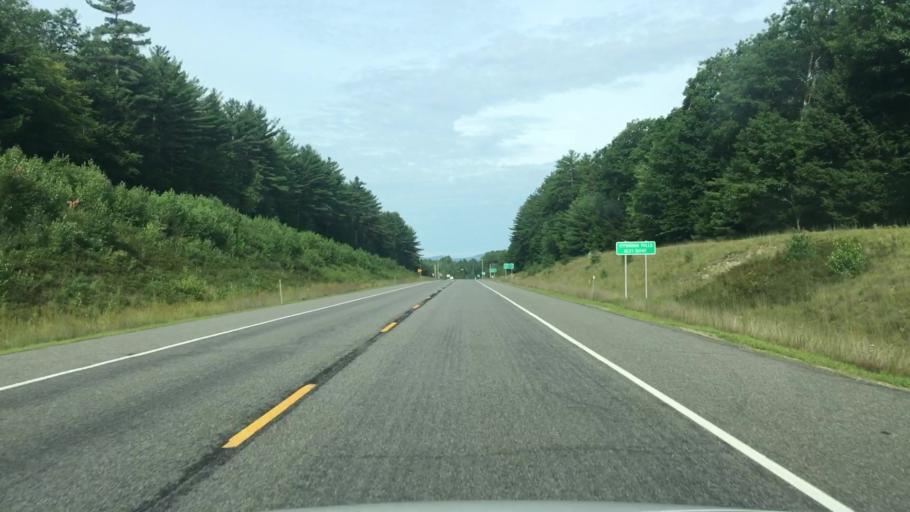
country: US
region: New Hampshire
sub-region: Carroll County
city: Freedom
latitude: 43.7922
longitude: -71.0464
